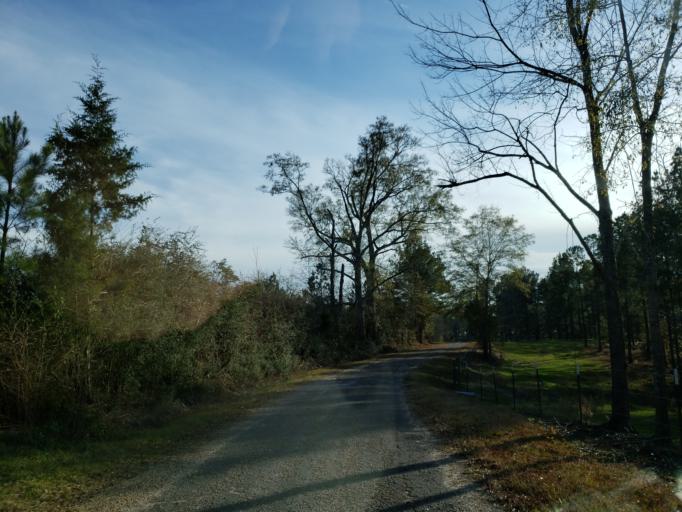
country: US
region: Mississippi
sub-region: Wayne County
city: Belmont
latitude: 31.4300
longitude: -88.4750
